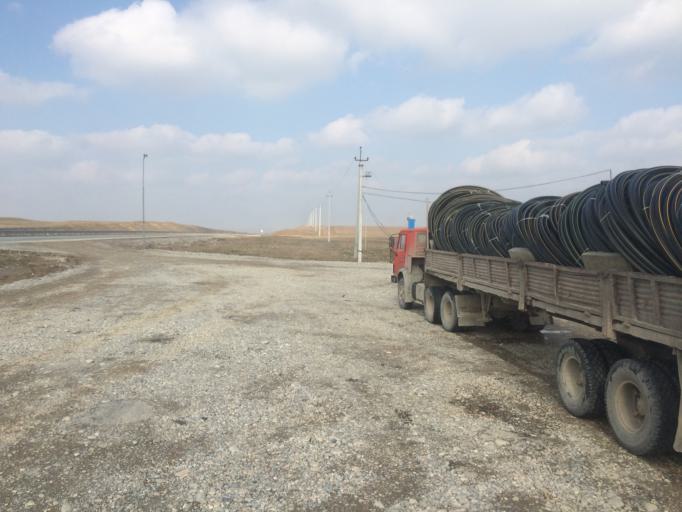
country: KZ
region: Ongtustik Qazaqstan
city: Temirlanovka
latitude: 42.5695
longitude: 69.3110
